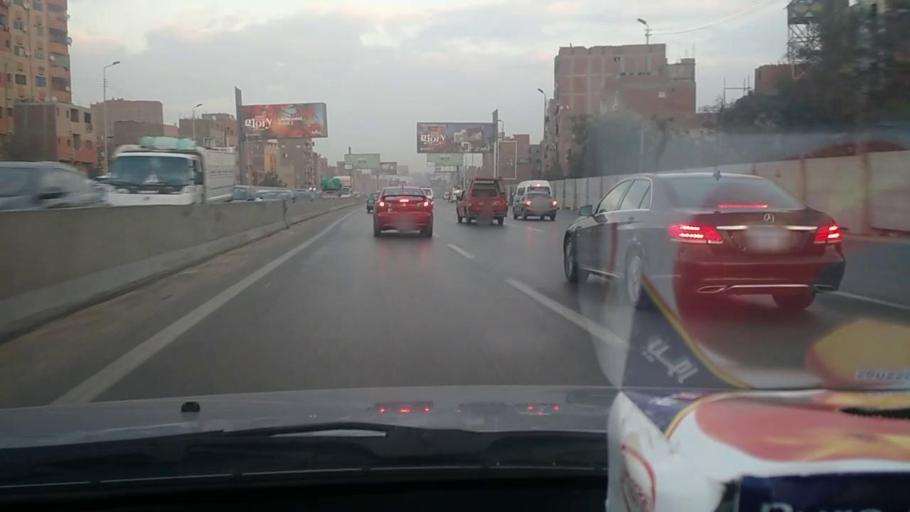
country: EG
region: Al Jizah
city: Al Jizah
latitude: 29.9923
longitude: 31.2484
